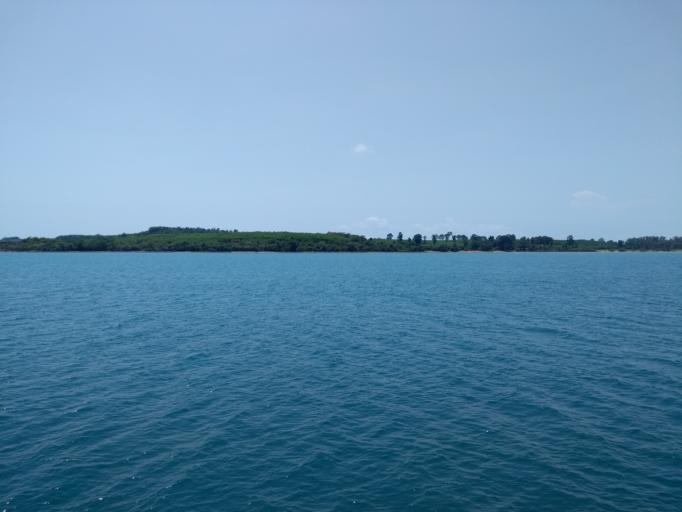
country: TH
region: Trat
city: Ko Kut
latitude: 11.8100
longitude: 102.5128
